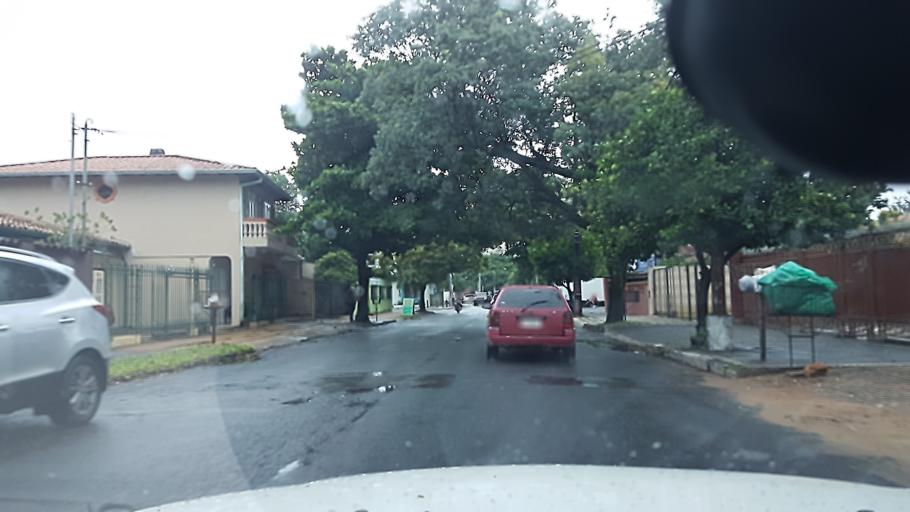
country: PY
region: Central
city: Fernando de la Mora
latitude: -25.2911
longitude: -57.5597
